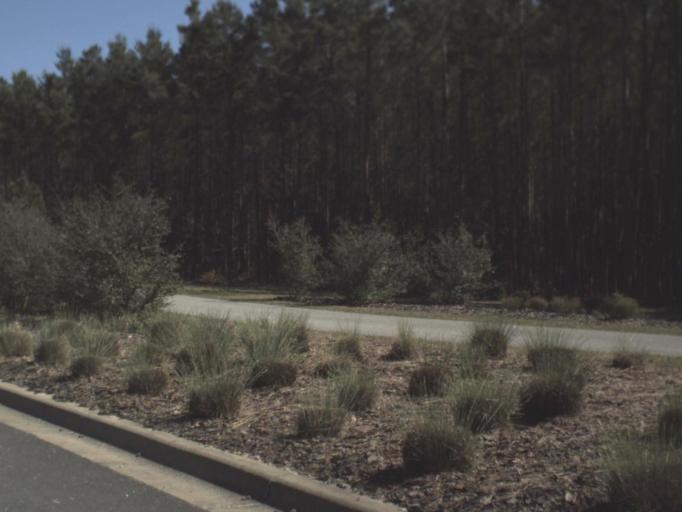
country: US
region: Florida
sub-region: Leon County
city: Woodville
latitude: 30.3756
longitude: -84.2644
